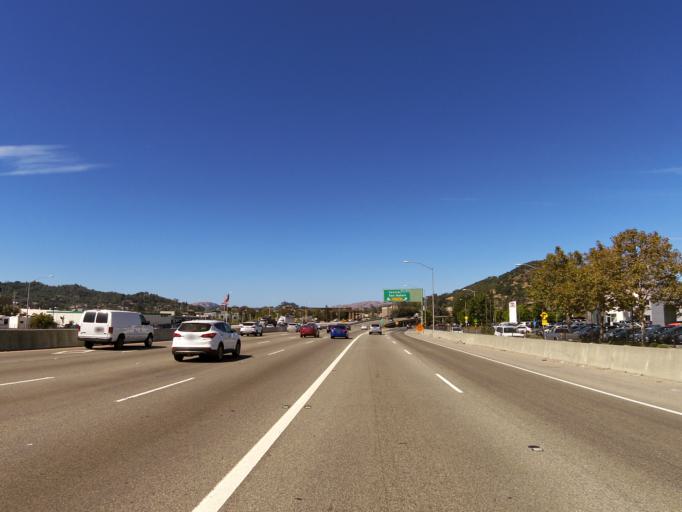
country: US
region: California
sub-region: Marin County
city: San Rafael
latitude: 37.9674
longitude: -122.5184
